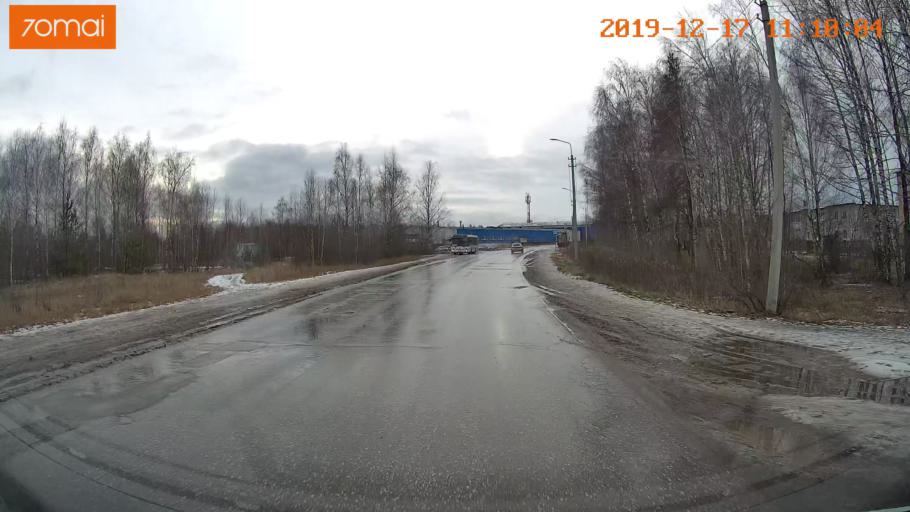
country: RU
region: Vladimir
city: Gus'-Khrustal'nyy
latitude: 55.5957
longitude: 40.6417
